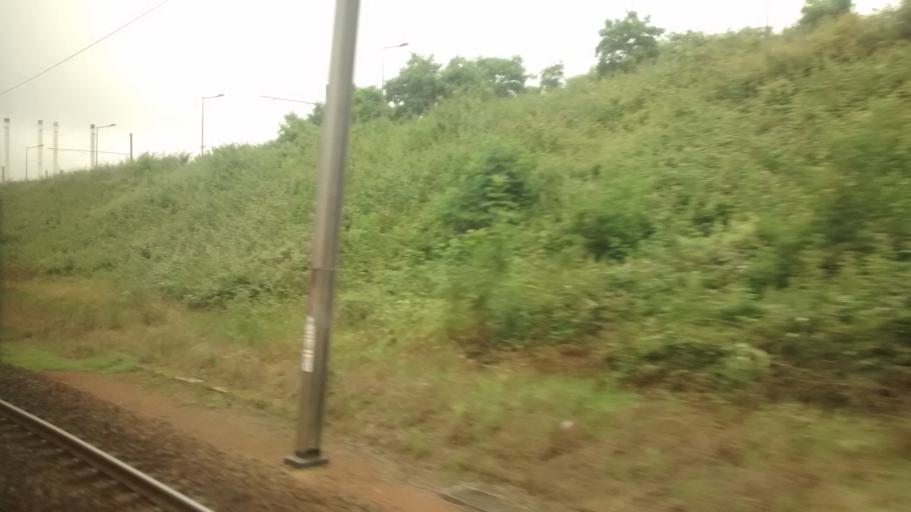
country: FR
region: Pays de la Loire
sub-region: Departement de la Sarthe
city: La Chapelle-Saint-Aubin
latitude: 48.0153
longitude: 0.1744
